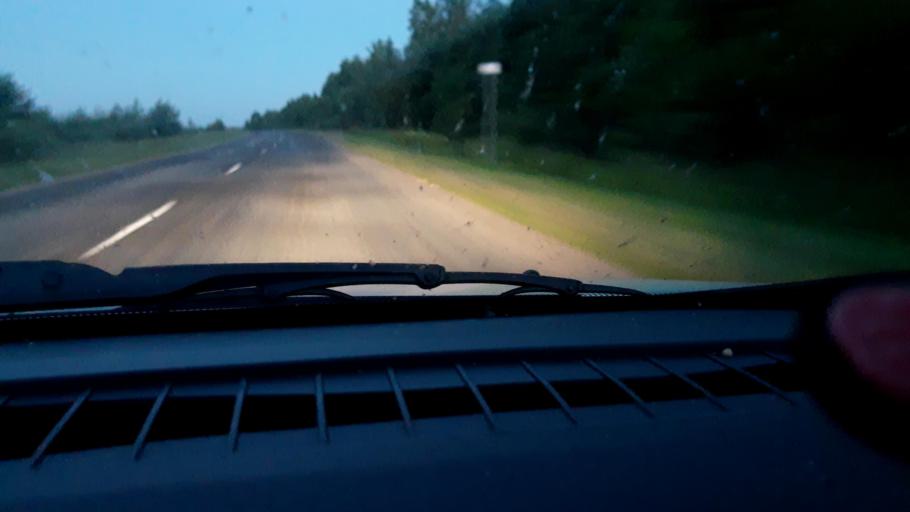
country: RU
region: Nizjnij Novgorod
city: Tonkino
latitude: 57.3625
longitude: 46.4247
